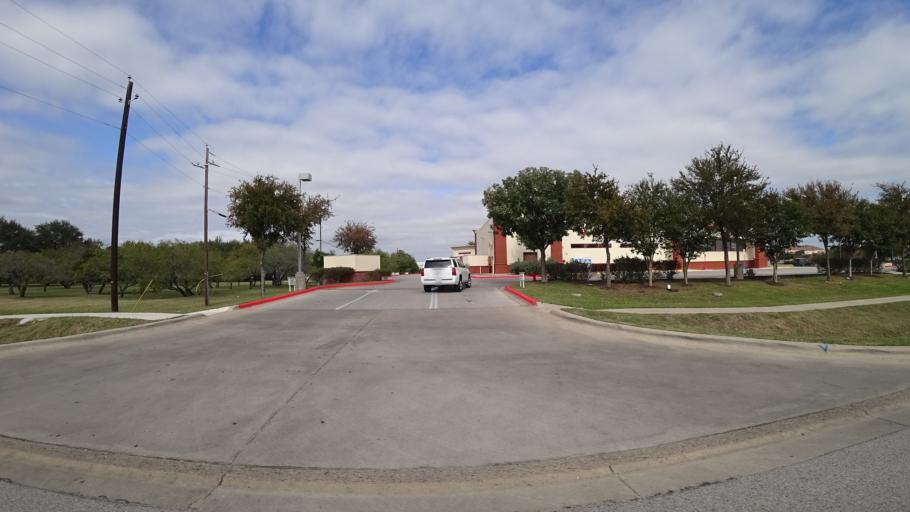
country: US
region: Texas
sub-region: Williamson County
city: Round Rock
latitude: 30.5359
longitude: -97.6961
